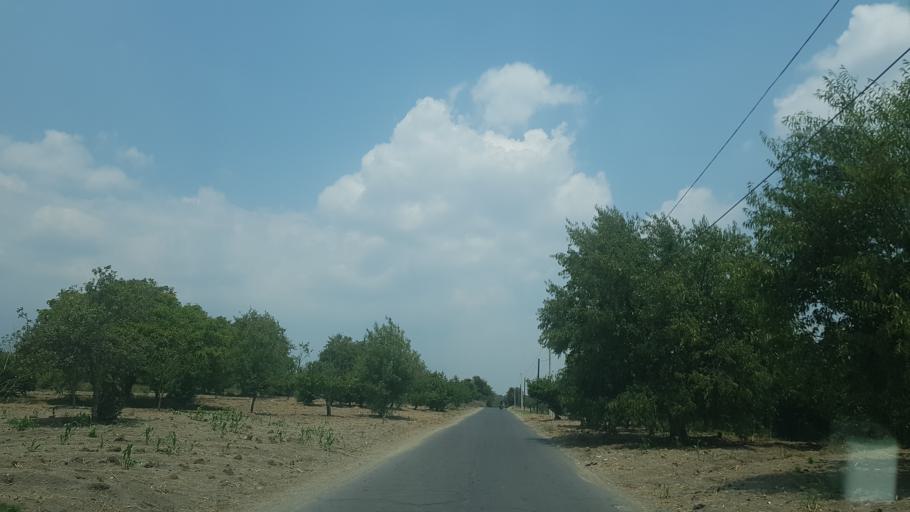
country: MX
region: Puebla
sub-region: San Nicolas de los Ranchos
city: San Pedro Yancuitlalpan
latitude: 19.0874
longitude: -98.4819
